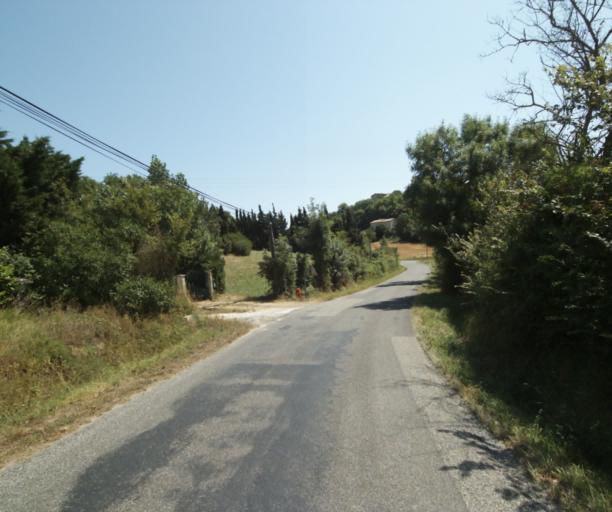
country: FR
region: Midi-Pyrenees
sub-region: Departement de la Haute-Garonne
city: Saint-Felix-Lauragais
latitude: 43.4520
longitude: 1.8891
